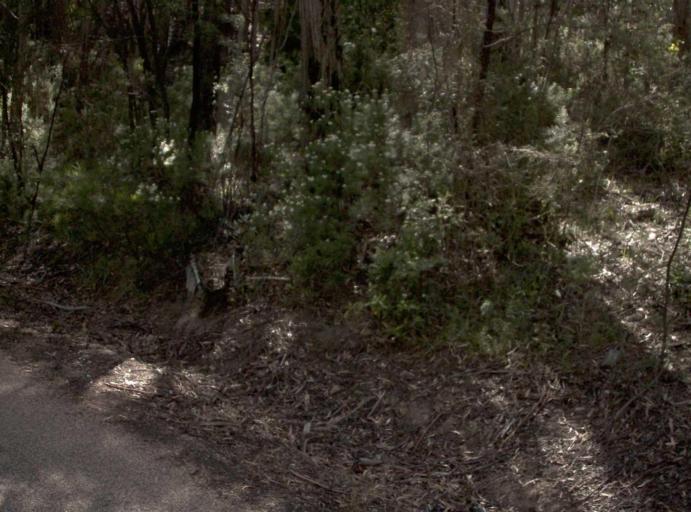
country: AU
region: Victoria
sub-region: East Gippsland
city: Lakes Entrance
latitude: -37.4105
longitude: 148.1227
